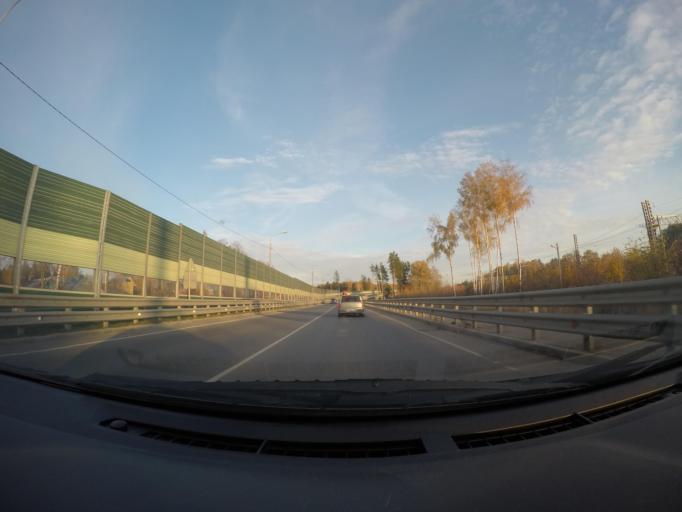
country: RU
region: Moskovskaya
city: Firsanovka
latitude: 55.9599
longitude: 37.2555
